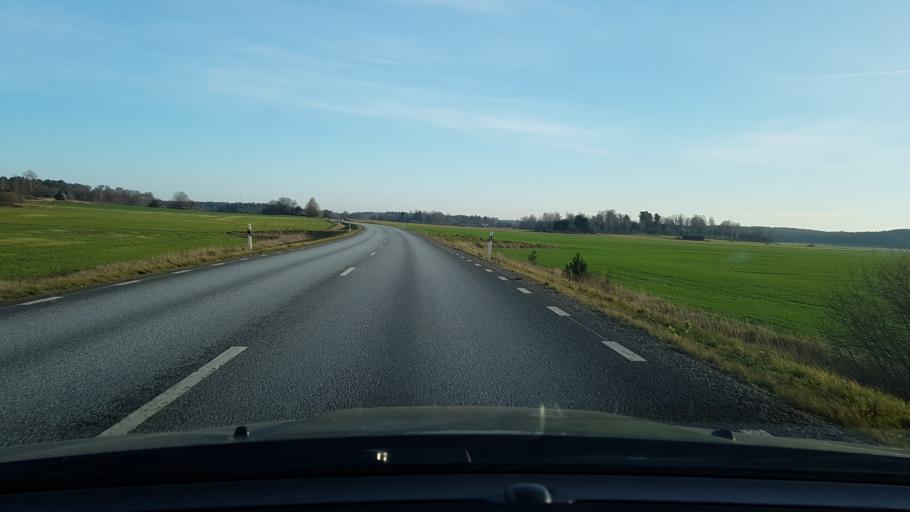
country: SE
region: Stockholm
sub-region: Vallentuna Kommun
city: Vallentuna
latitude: 59.7503
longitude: 18.0499
